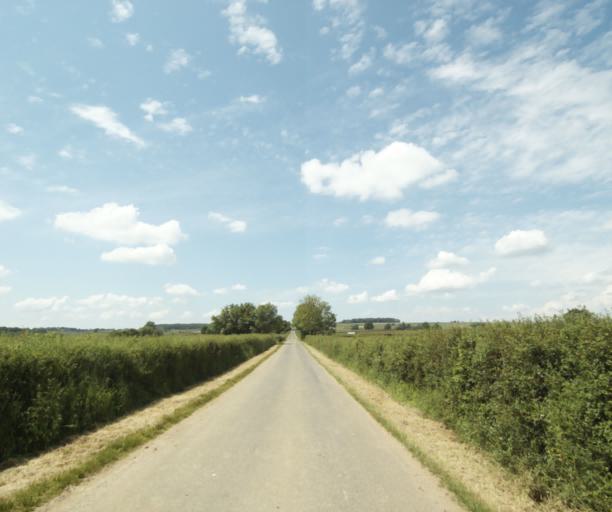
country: FR
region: Bourgogne
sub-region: Departement de Saone-et-Loire
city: Perrecy-les-Forges
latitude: 46.5784
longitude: 4.1529
